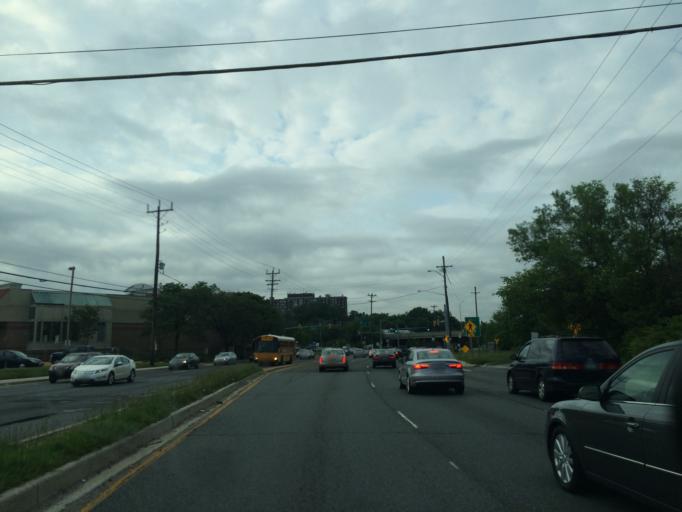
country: US
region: Maryland
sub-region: Montgomery County
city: Hillandale
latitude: 39.0215
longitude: -76.9771
